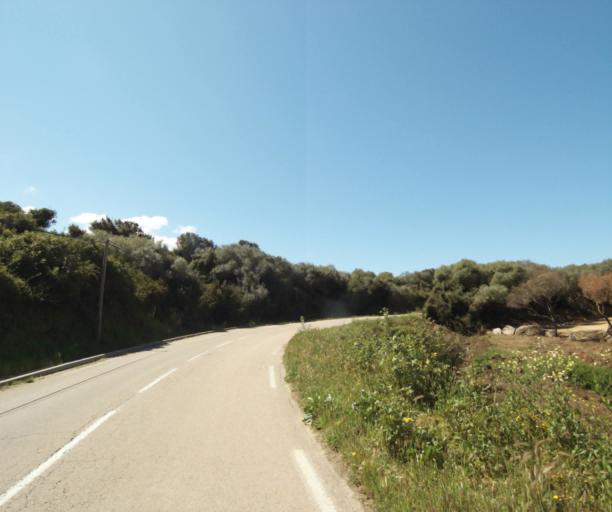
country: FR
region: Corsica
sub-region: Departement de la Corse-du-Sud
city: Propriano
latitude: 41.6574
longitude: 8.8962
